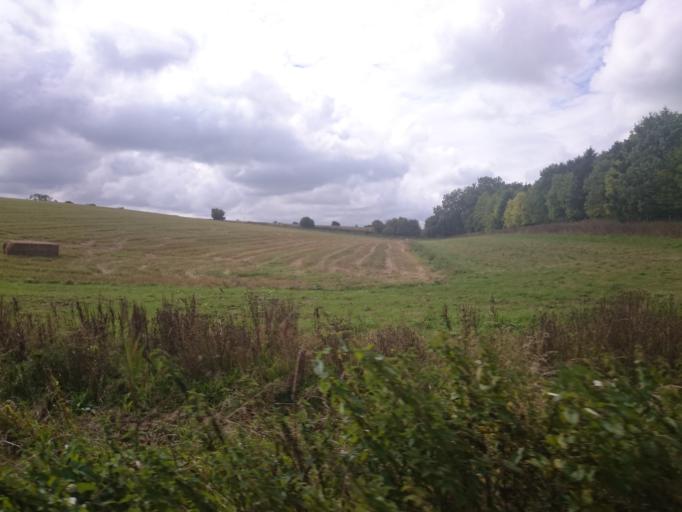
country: GB
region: England
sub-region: Gloucestershire
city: Coates
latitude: 51.7681
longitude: -2.0465
